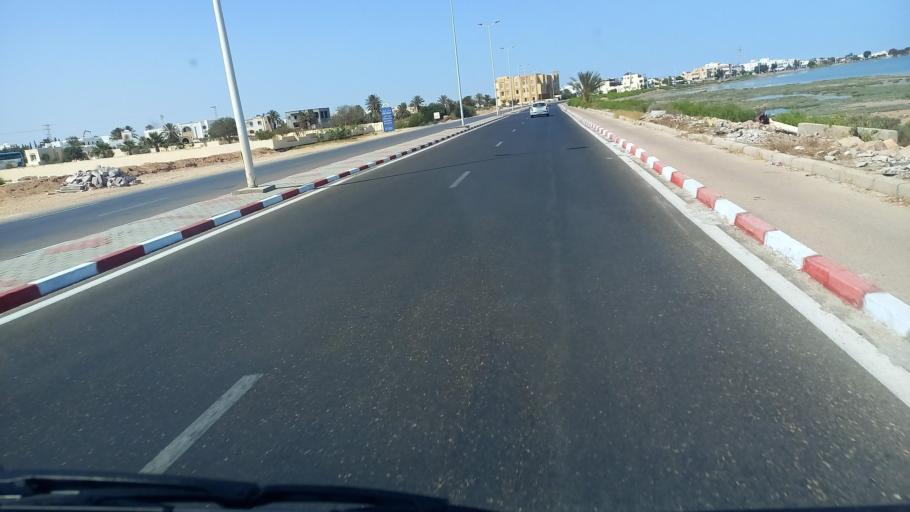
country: TN
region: Madanin
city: Houmt Souk
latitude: 33.8744
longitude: 10.9016
